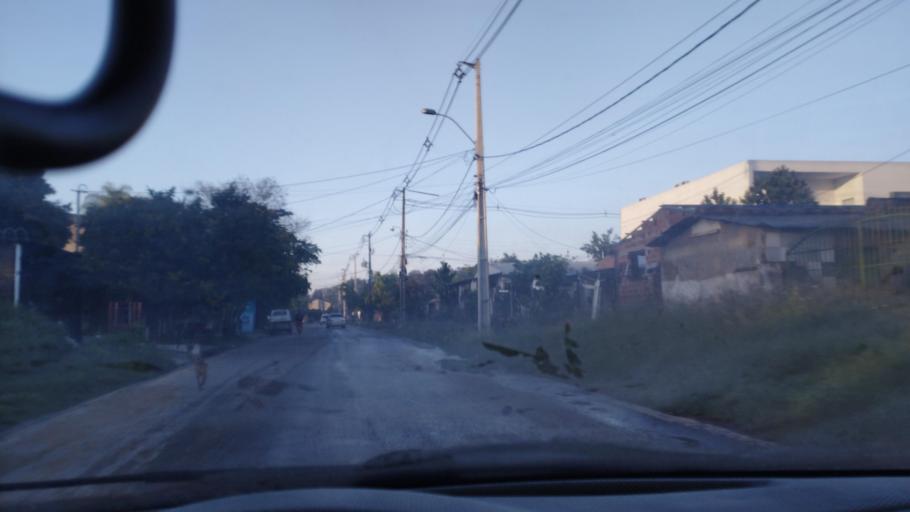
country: PY
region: Central
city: Fernando de la Mora
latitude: -25.2935
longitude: -57.5418
